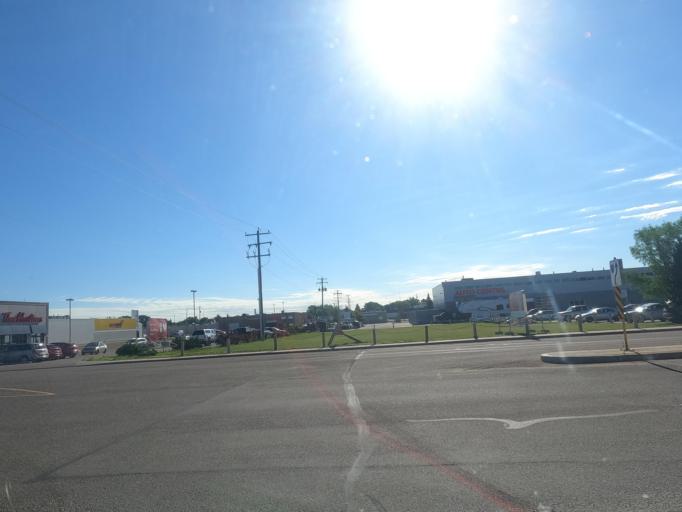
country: CA
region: Alberta
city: Brooks
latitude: 50.5734
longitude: -111.9009
